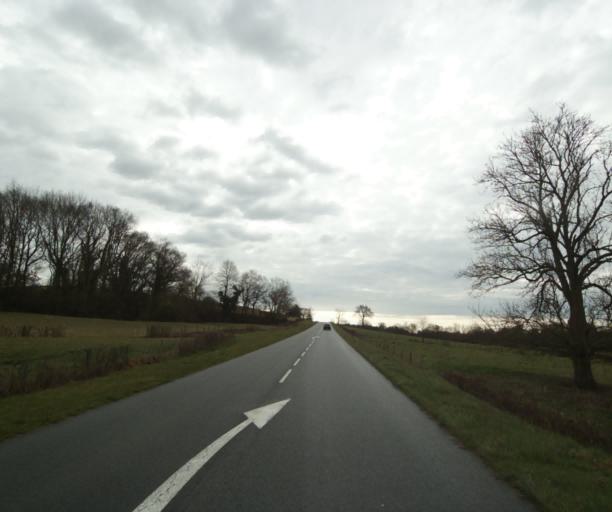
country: FR
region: Auvergne
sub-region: Departement de l'Allier
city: Toulon-sur-Allier
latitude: 46.4951
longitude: 3.3911
